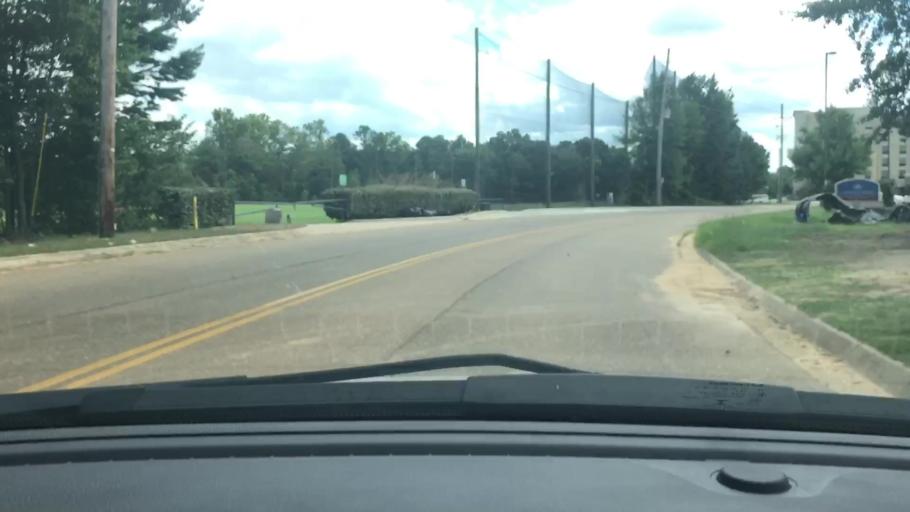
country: US
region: Arkansas
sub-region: Miller County
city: Texarkana
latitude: 33.4599
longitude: -94.0741
